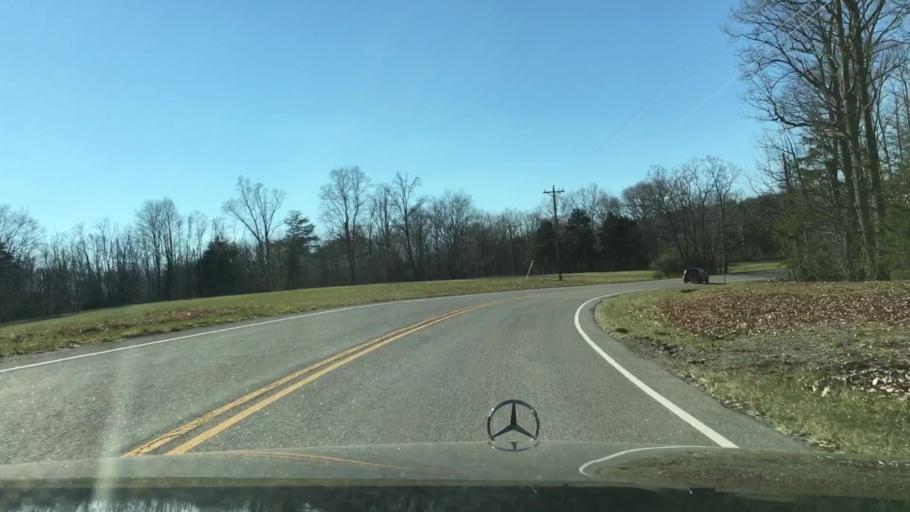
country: US
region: Virginia
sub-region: City of Bedford
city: Bedford
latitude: 37.2218
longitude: -79.5070
